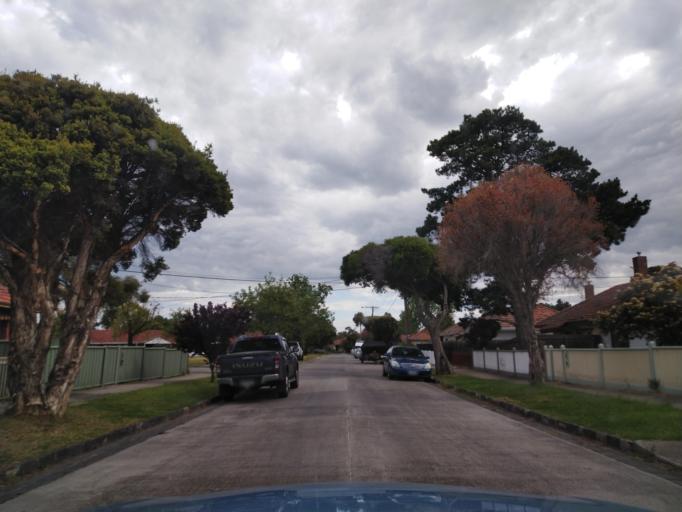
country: AU
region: Victoria
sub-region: Hobsons Bay
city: Williamstown North
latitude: -37.8542
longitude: 144.8824
